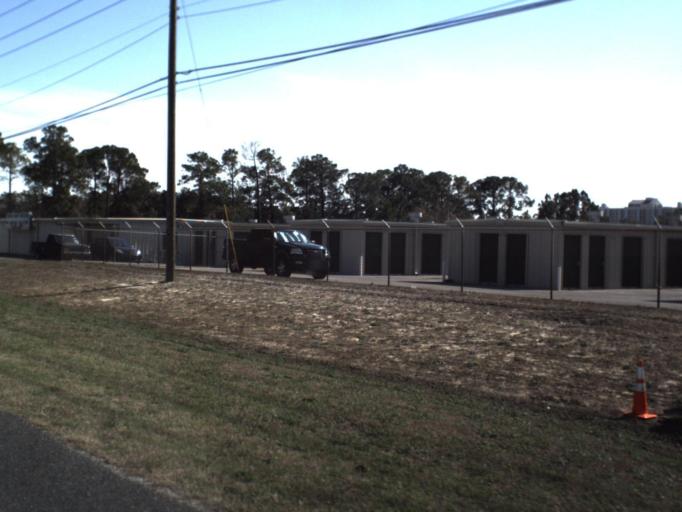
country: US
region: Florida
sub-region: Bay County
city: Laguna Beach
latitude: 30.2361
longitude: -85.9044
